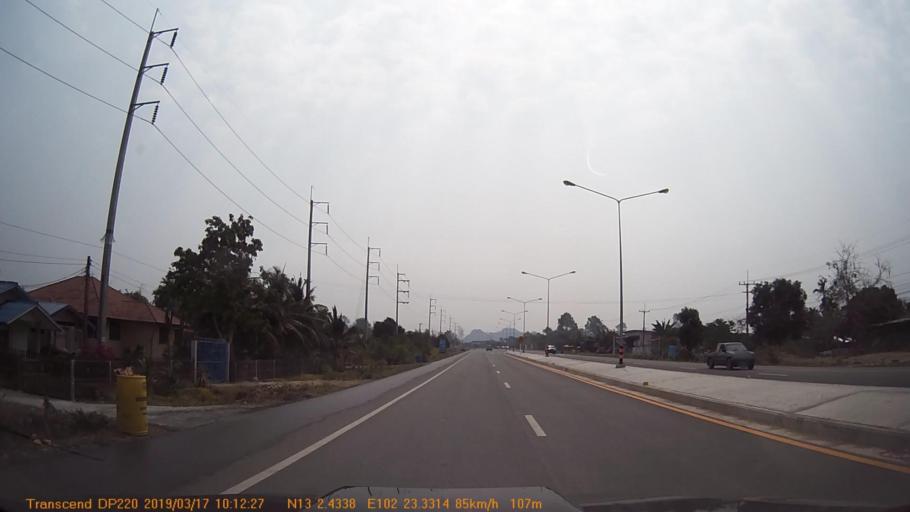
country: TH
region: Chanthaburi
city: Pong Nam Ron
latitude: 13.0400
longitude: 102.3914
